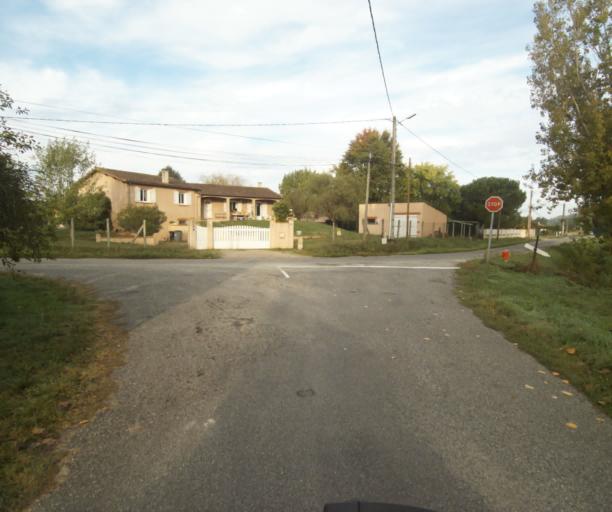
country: FR
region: Midi-Pyrenees
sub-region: Departement du Tarn-et-Garonne
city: Montech
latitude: 43.9651
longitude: 1.2301
